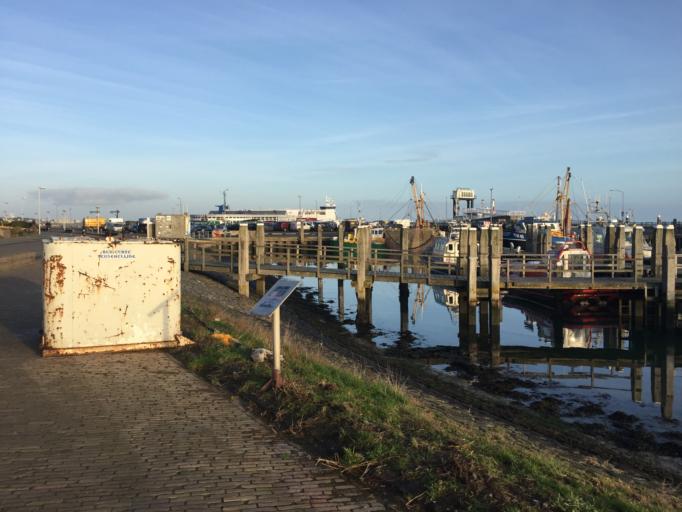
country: NL
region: Friesland
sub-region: Gemeente Terschelling
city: West-Terschelling
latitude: 53.3567
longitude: 5.2141
